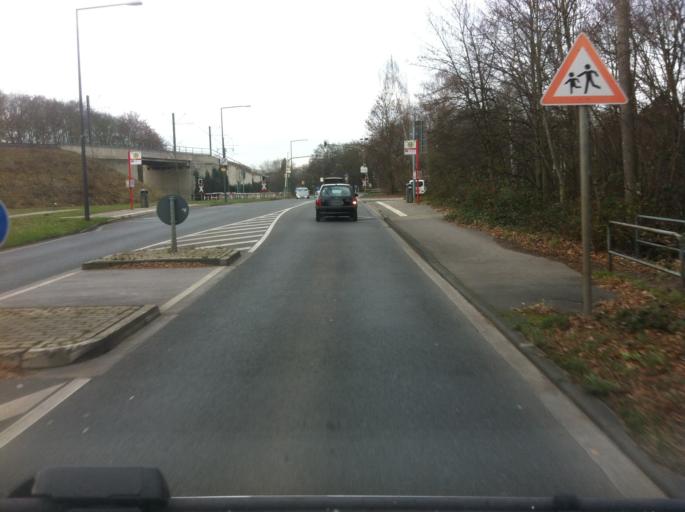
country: DE
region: North Rhine-Westphalia
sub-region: Regierungsbezirk Koln
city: Bilderstoeckchen
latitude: 50.9773
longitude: 6.9044
